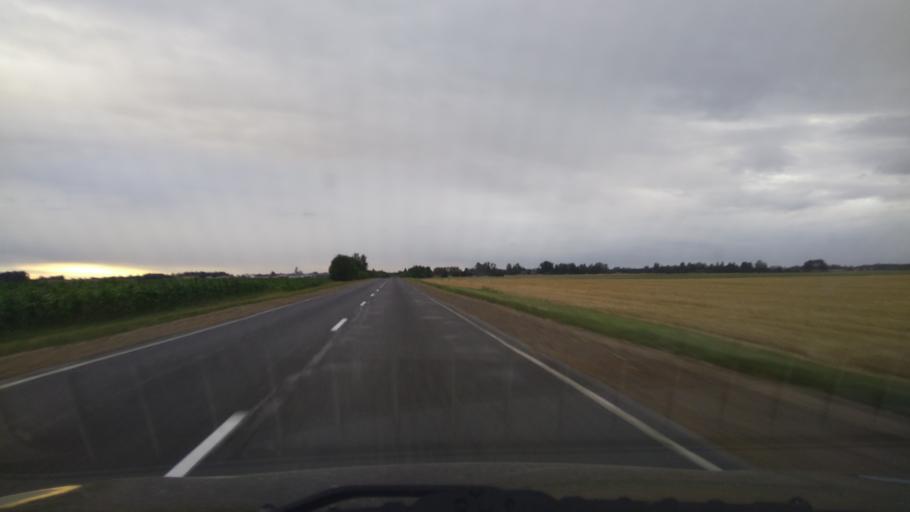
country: BY
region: Brest
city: Byaroza
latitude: 52.4415
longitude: 24.9758
